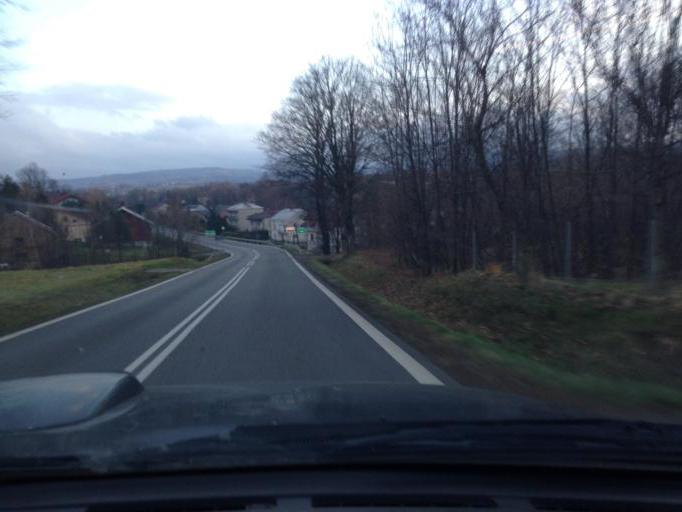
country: PL
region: Subcarpathian Voivodeship
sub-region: Powiat jasielski
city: Nowy Zmigrod
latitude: 49.6251
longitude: 21.5353
